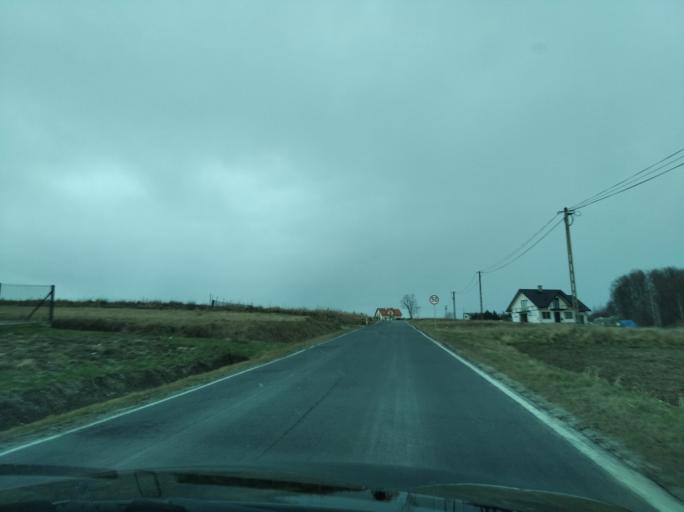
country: PL
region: Subcarpathian Voivodeship
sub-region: Powiat rzeszowski
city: Hyzne
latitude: 49.9178
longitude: 22.1979
